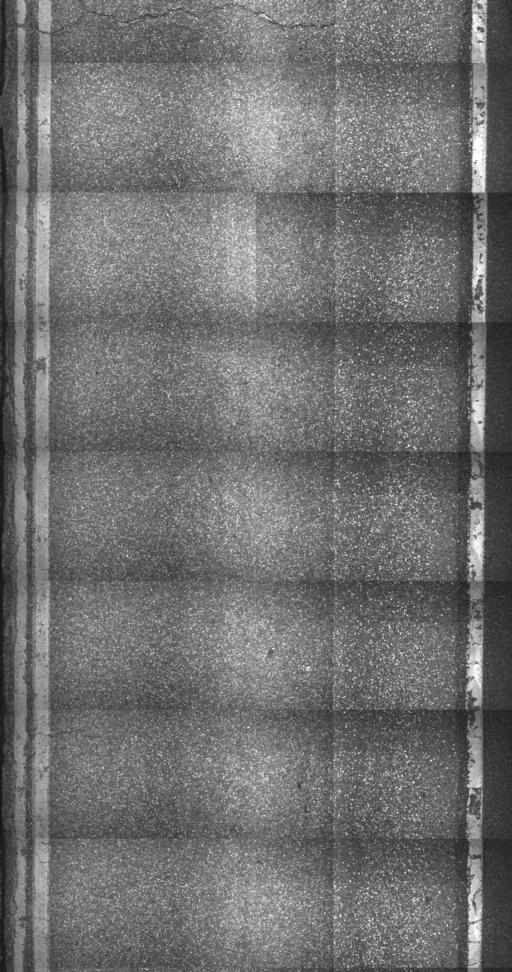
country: US
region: Vermont
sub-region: Washington County
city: Waterbury
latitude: 44.3673
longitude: -72.7296
